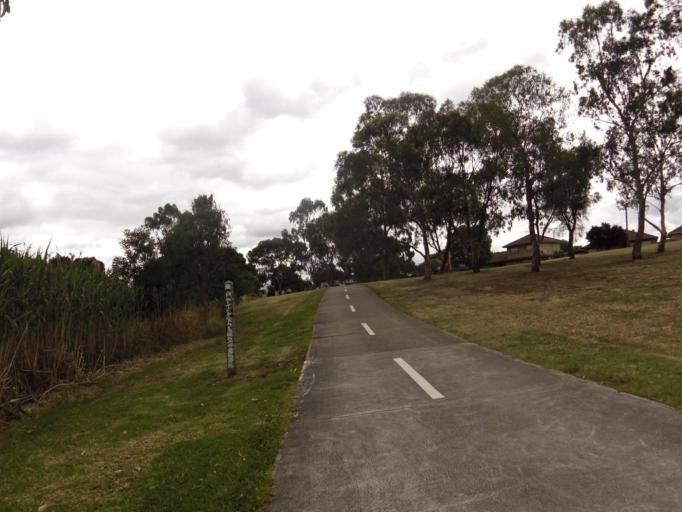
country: AU
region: Victoria
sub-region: Darebin
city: Kingsbury
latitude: -37.7181
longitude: 145.0307
